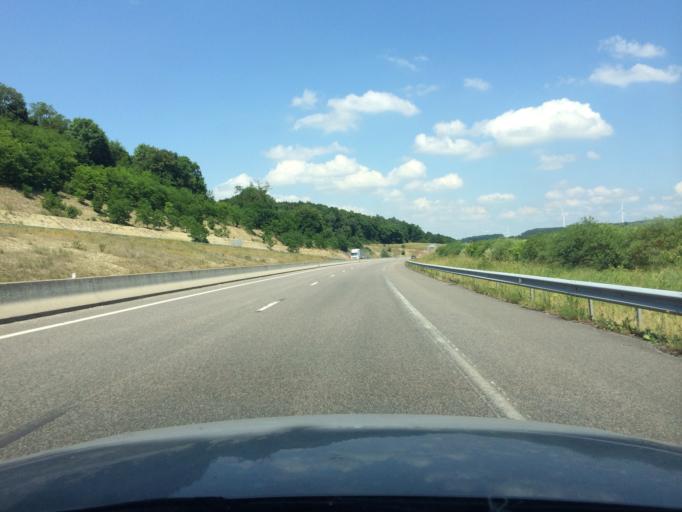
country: FR
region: Lorraine
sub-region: Departement de la Moselle
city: Lorquin
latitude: 48.6029
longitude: 6.8465
